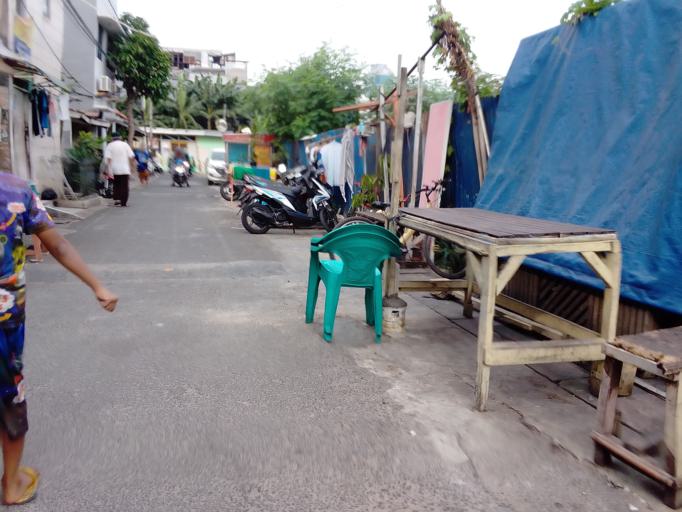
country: ID
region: Jakarta Raya
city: Jakarta
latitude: -6.1805
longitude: 106.8153
